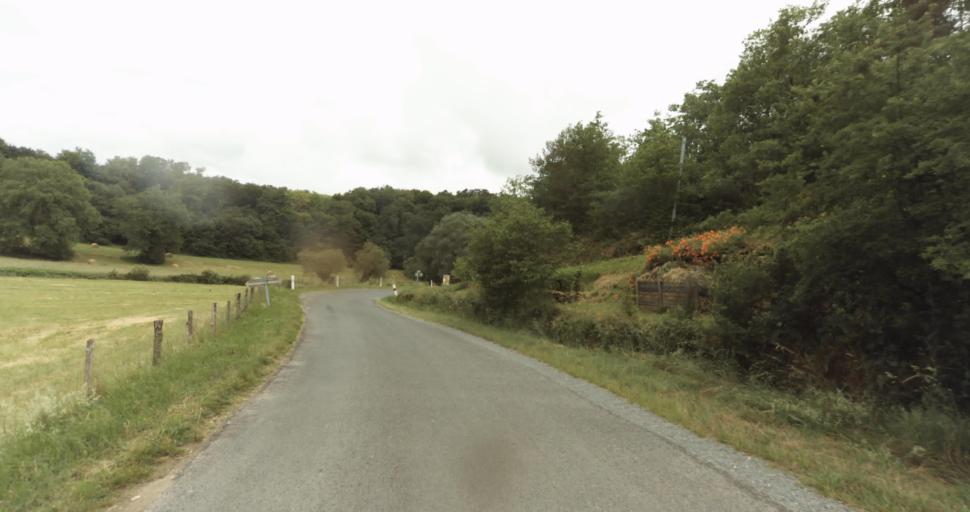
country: FR
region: Aquitaine
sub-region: Departement de la Dordogne
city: Belves
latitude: 44.7604
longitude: 0.9054
